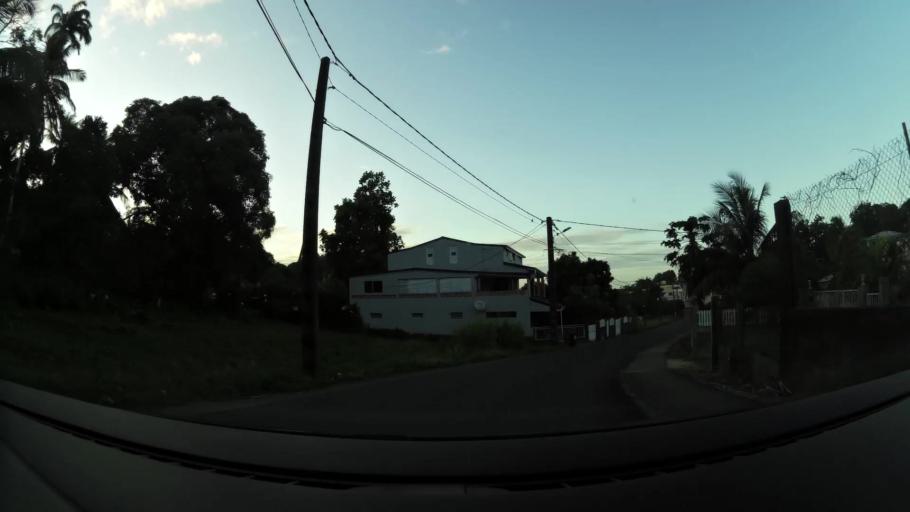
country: GP
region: Guadeloupe
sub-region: Guadeloupe
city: Les Abymes
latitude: 16.2722
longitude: -61.4982
